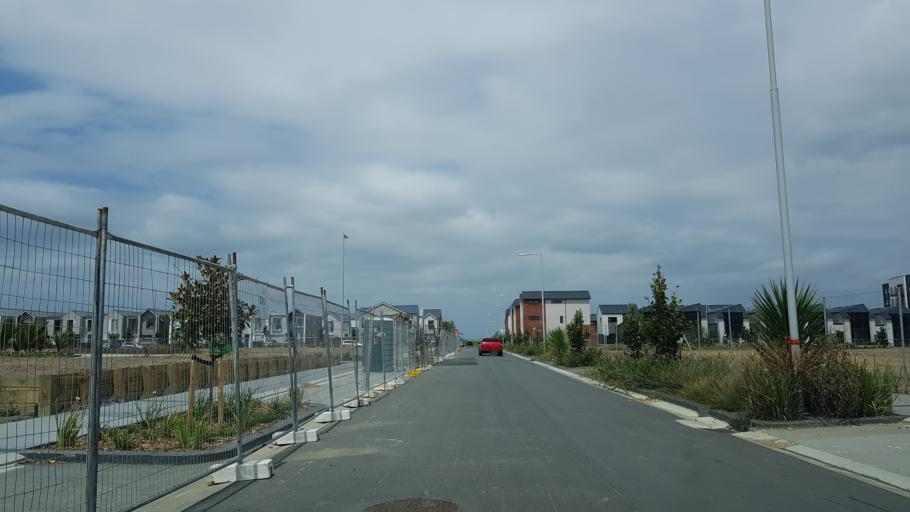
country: NZ
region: Auckland
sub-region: Auckland
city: Rosebank
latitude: -36.7905
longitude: 174.6644
